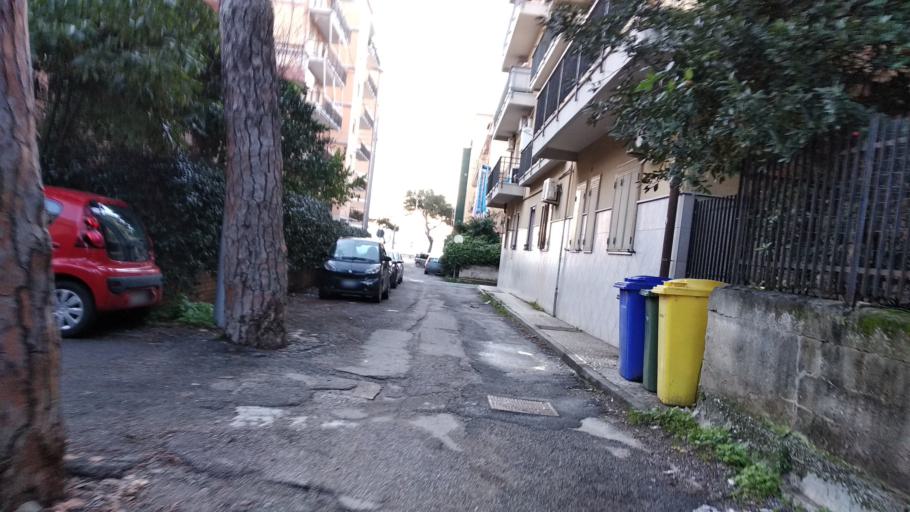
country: IT
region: Calabria
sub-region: Provincia di Catanzaro
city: Barone
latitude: 38.8278
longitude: 16.6260
